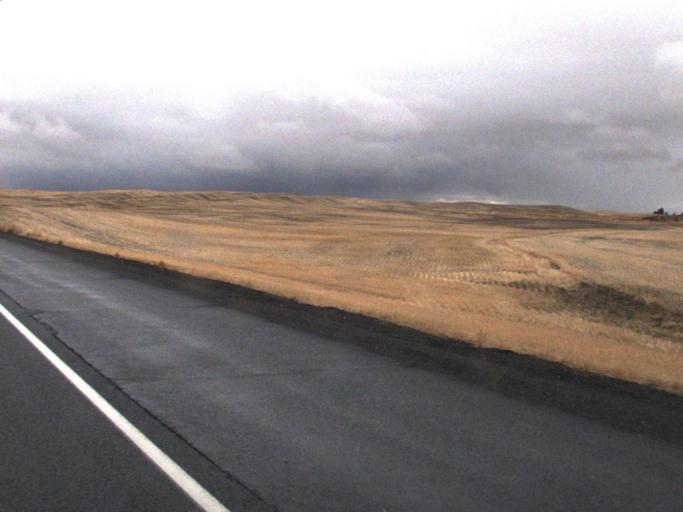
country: US
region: Washington
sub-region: Spokane County
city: Cheney
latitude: 47.4168
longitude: -117.3916
